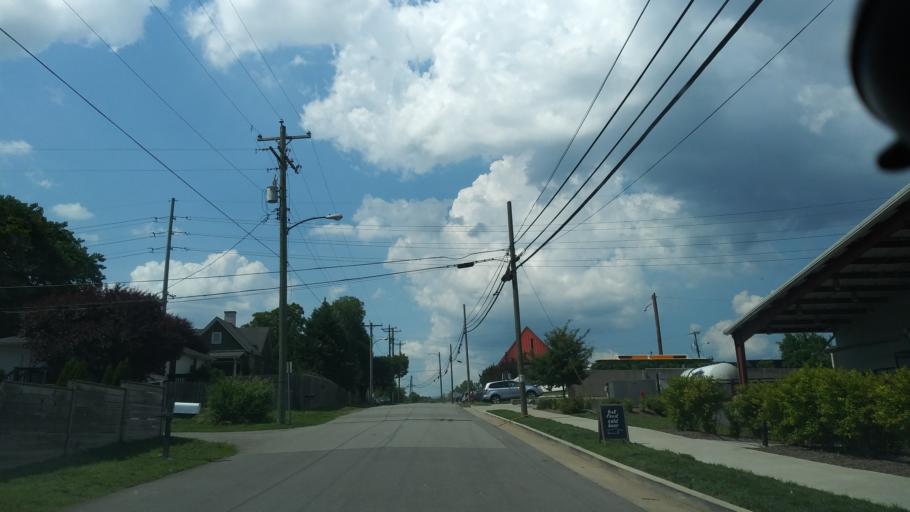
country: US
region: Tennessee
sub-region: Davidson County
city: Nashville
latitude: 36.1571
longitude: -86.8398
